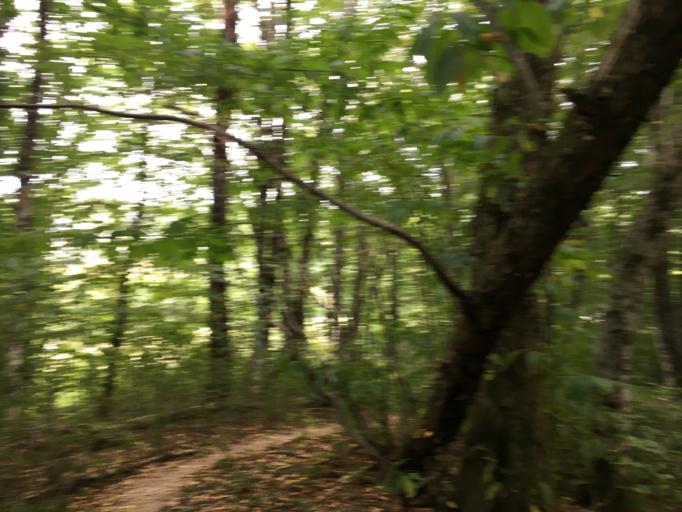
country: RU
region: Krasnodarskiy
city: Tuapse
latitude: 44.2514
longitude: 39.2298
